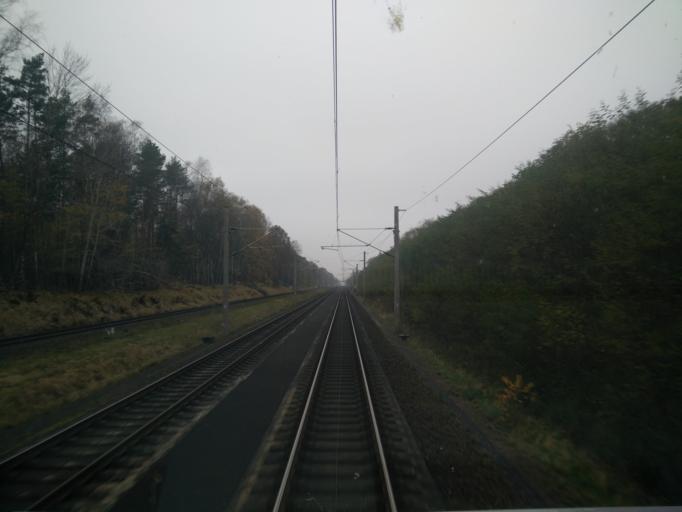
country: DE
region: Brandenburg
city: Retzow
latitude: 52.5897
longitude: 12.7230
